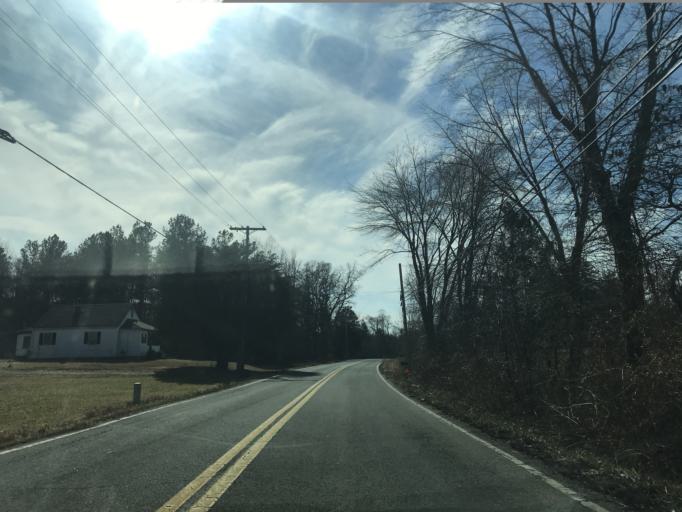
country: US
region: Maryland
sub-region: Charles County
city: Indian Head
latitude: 38.5463
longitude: -77.1309
